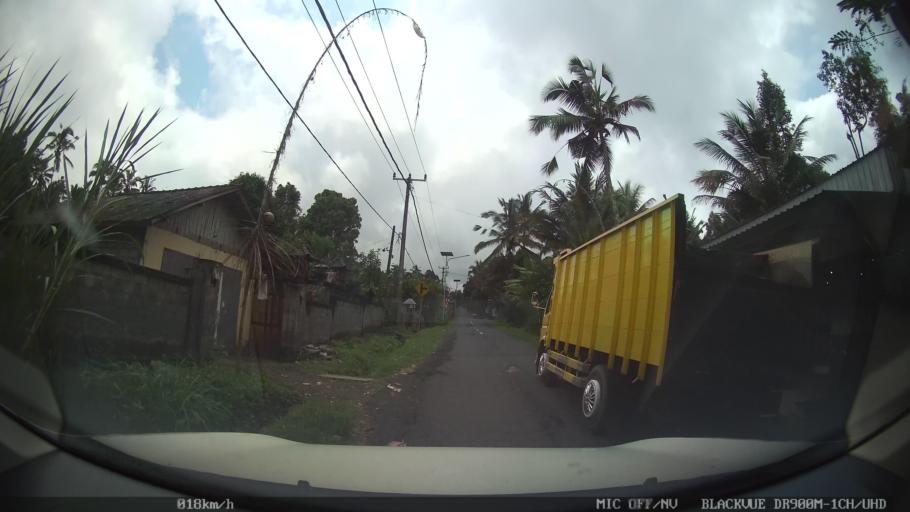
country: ID
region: Bali
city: Banjar Geriana Kangin
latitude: -8.4078
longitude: 115.4393
